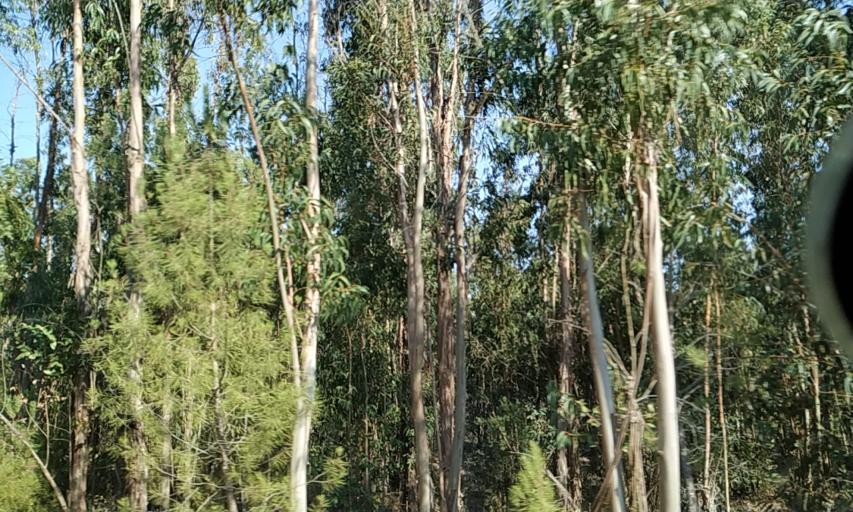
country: PT
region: Evora
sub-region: Vendas Novas
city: Vendas Novas
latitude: 38.7830
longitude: -8.5857
